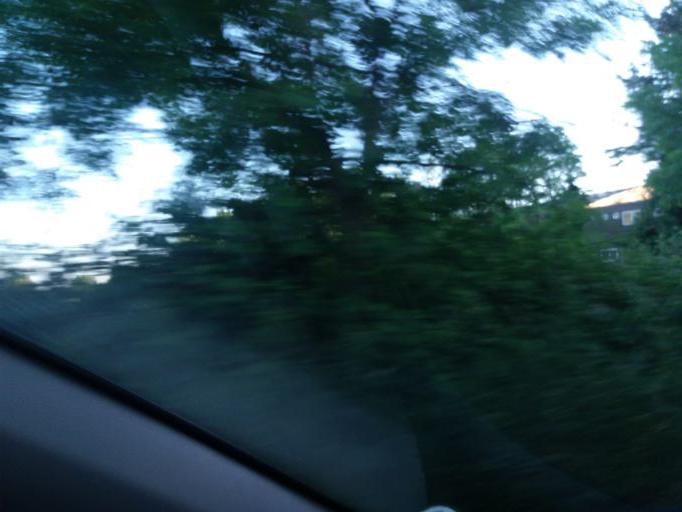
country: IE
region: Leinster
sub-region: Dublin City
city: Finglas
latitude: 53.4497
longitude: -6.3257
